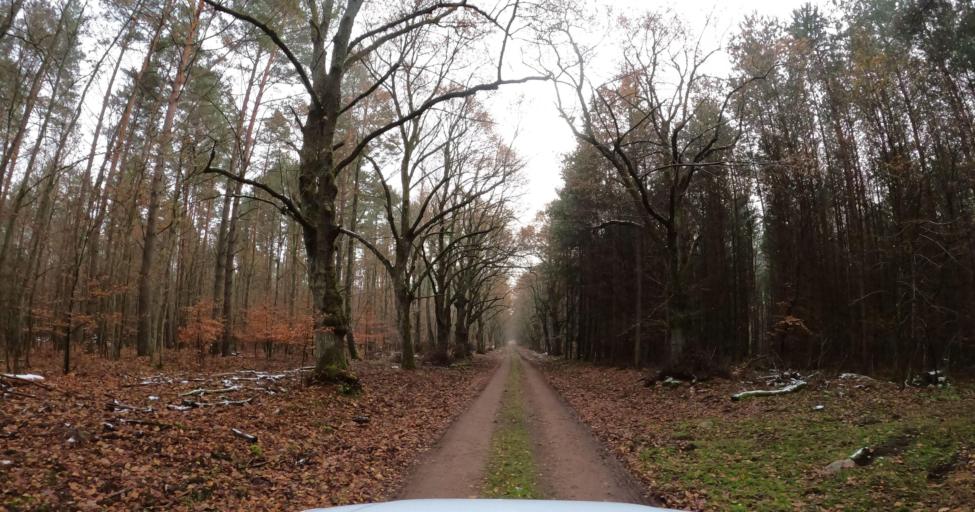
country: PL
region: West Pomeranian Voivodeship
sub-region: Powiat swidwinski
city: Rabino
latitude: 53.8990
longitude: 15.8960
